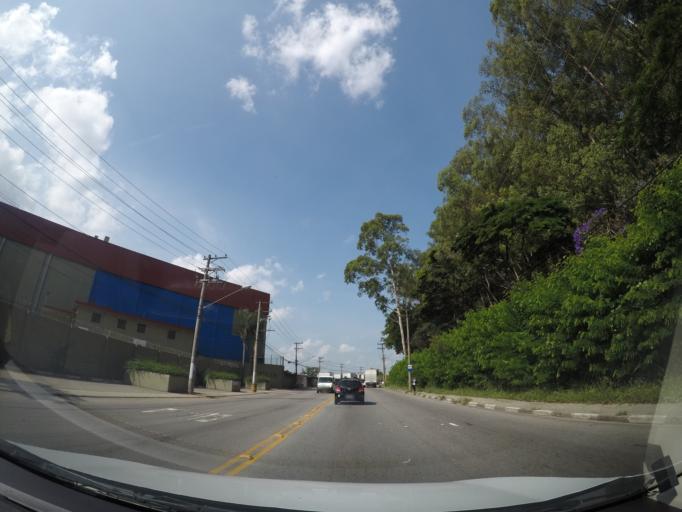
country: BR
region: Sao Paulo
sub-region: Guarulhos
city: Guarulhos
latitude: -23.4365
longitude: -46.4572
